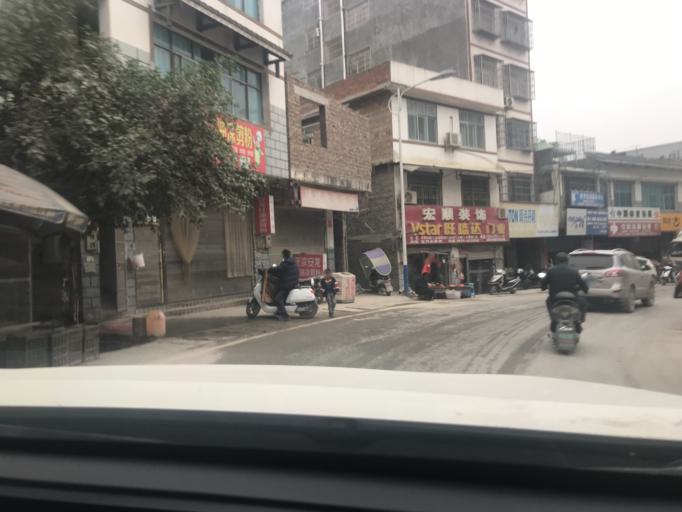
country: CN
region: Guangxi Zhuangzu Zizhiqu
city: Xinzhou
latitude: 24.9830
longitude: 105.8083
